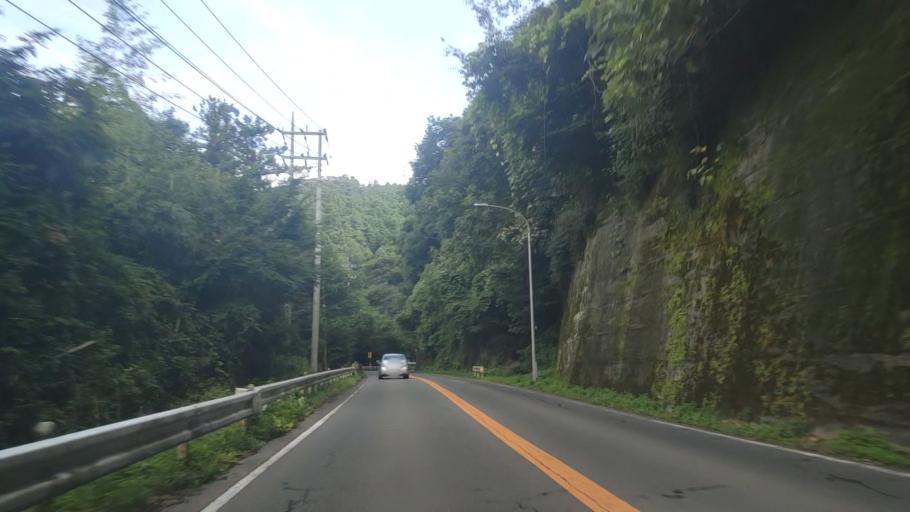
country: JP
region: Gunma
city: Omamacho-omama
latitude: 36.4553
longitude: 139.2655
